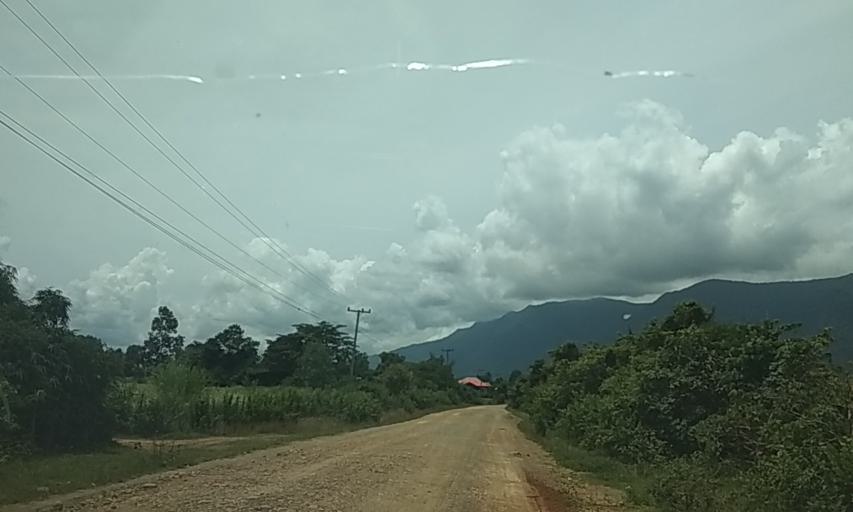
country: LA
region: Bolikhamxai
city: Ban Nahin
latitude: 18.1428
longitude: 104.7565
